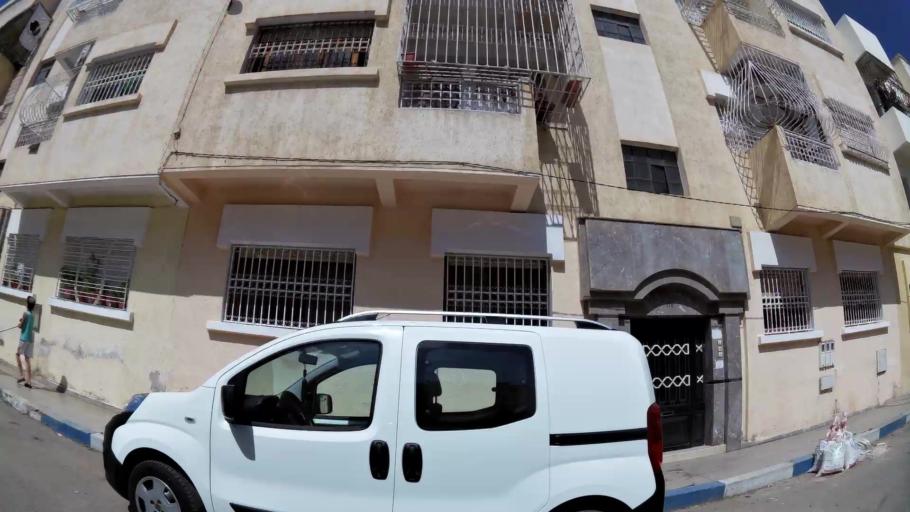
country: MA
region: Fes-Boulemane
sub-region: Fes
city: Fes
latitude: 34.0387
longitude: -5.0297
